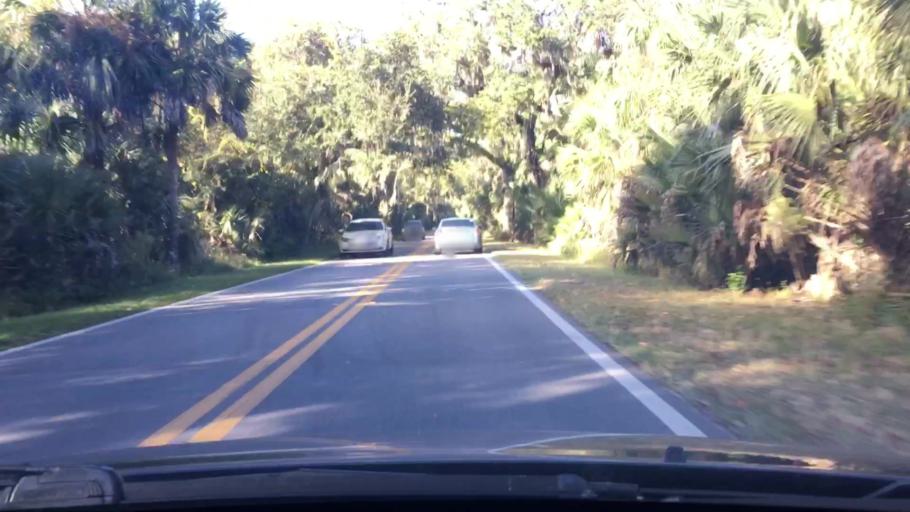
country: US
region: Florida
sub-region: Volusia County
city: Ormond-by-the-Sea
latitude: 29.3899
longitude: -81.1330
